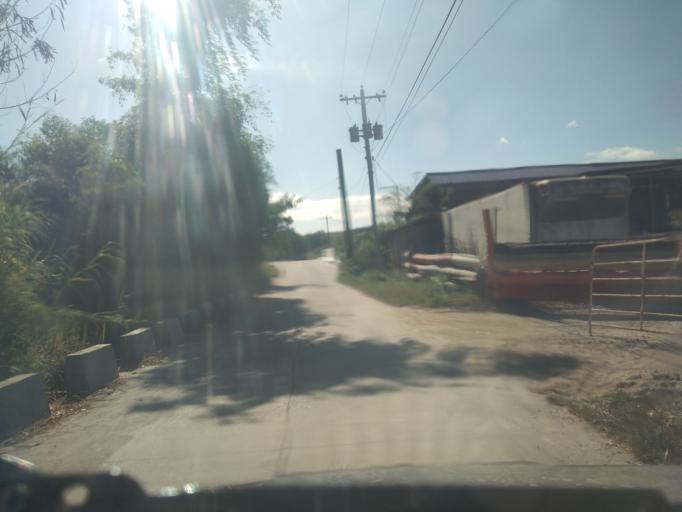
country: PH
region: Central Luzon
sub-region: Province of Pampanga
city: Calibutbut
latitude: 15.0939
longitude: 120.5925
